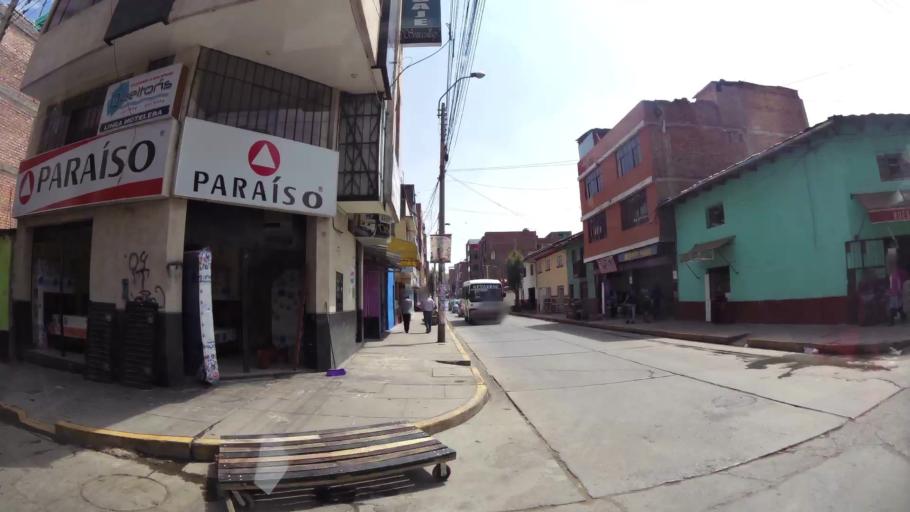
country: PE
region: Junin
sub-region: Provincia de Huancayo
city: El Tambo
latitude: -12.0727
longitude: -75.2121
